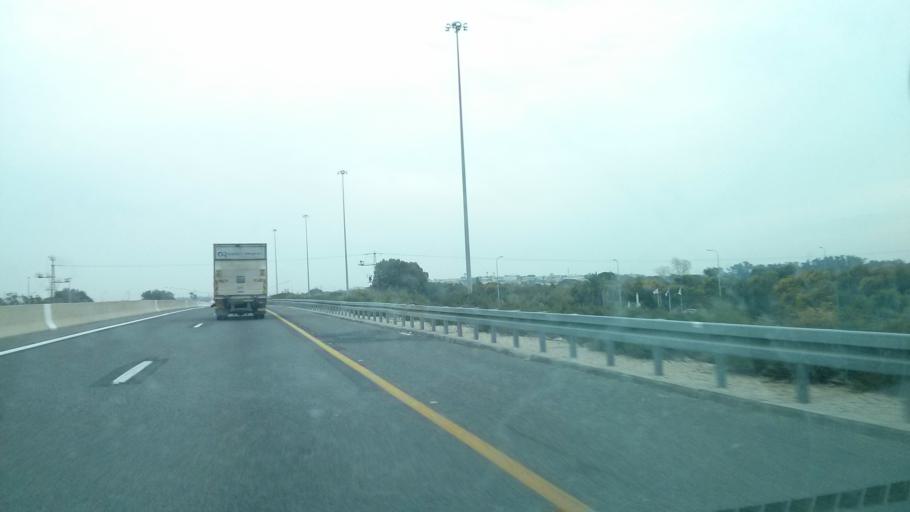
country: IL
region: Haifa
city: Qesarya
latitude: 32.5066
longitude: 34.9136
